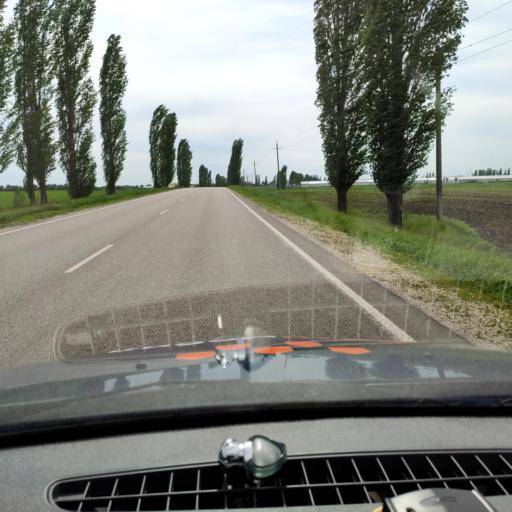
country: RU
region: Voronezj
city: Novaya Usman'
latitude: 51.5498
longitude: 39.3670
